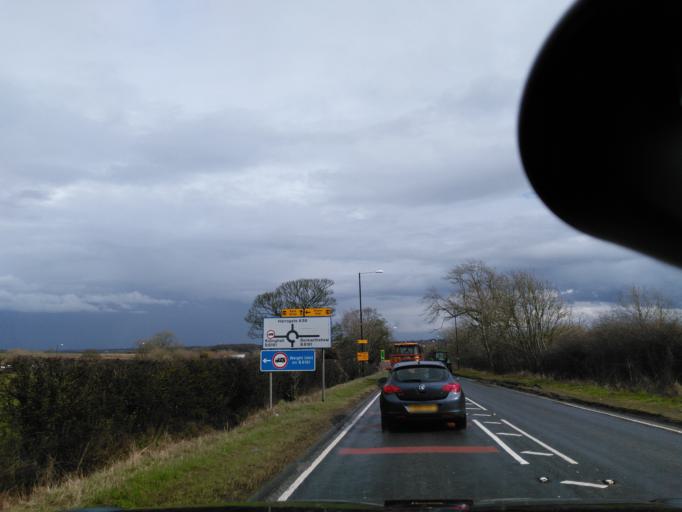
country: GB
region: England
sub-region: North Yorkshire
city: Harrogate
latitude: 54.0081
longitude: -1.5808
